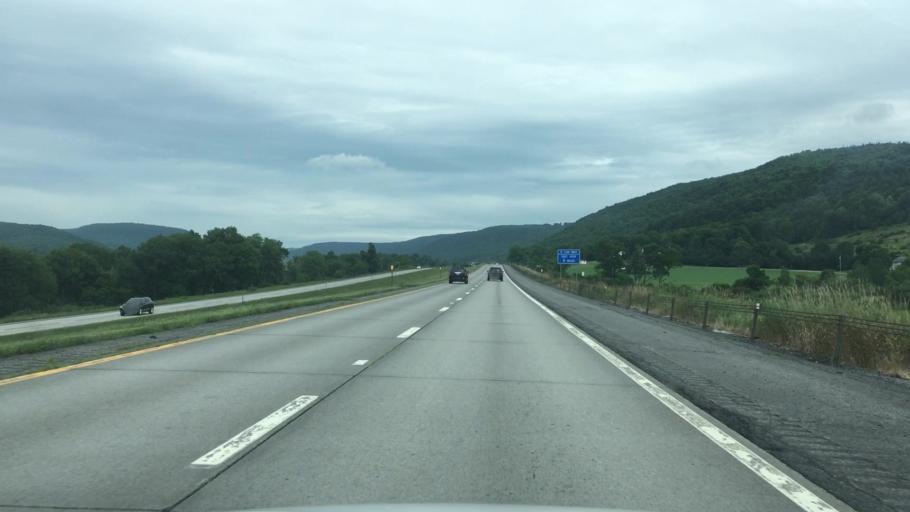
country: US
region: New York
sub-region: Otsego County
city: Worcester
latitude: 42.5343
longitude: -74.8545
